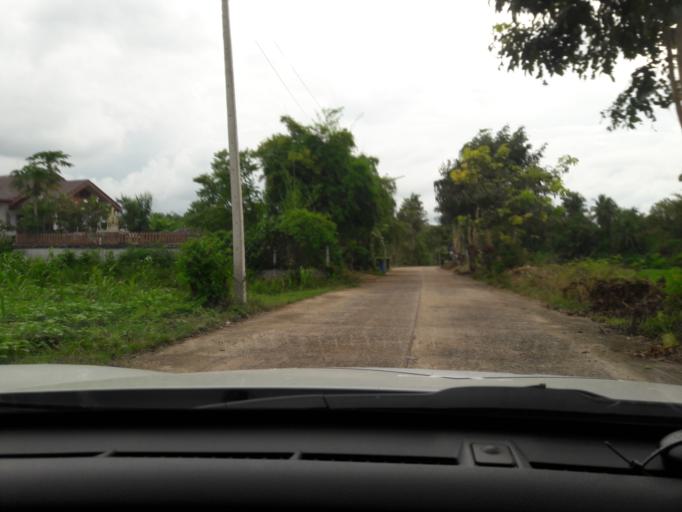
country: TH
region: Nakhon Sawan
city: Tak Fa
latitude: 15.3546
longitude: 100.4985
